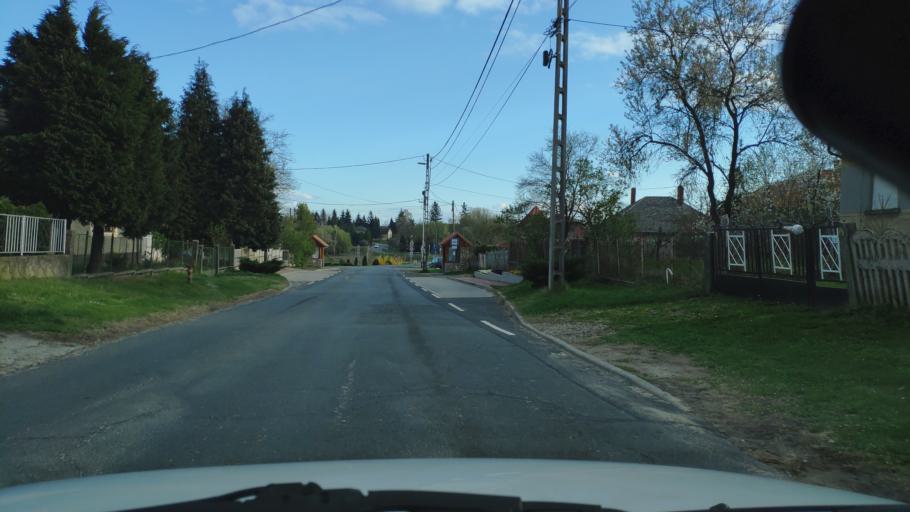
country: HU
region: Zala
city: Zalakomar
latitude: 46.4898
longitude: 17.1287
